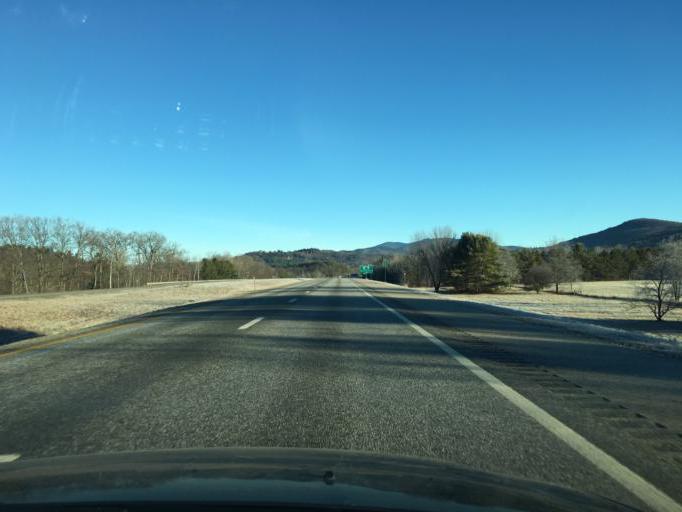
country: US
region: New Hampshire
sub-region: Grafton County
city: Thornton
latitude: 43.8313
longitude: -71.6548
